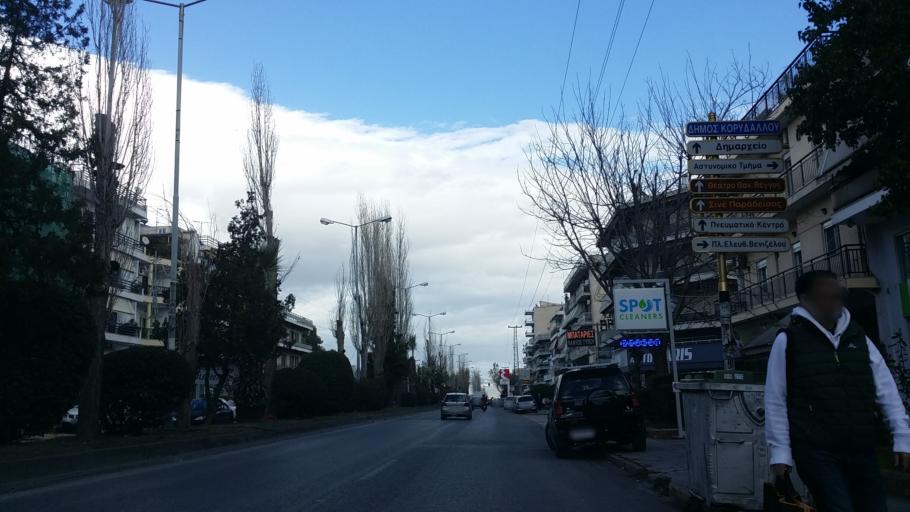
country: GR
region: Attica
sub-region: Nomos Piraios
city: Korydallos
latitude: 37.9795
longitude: 23.6437
